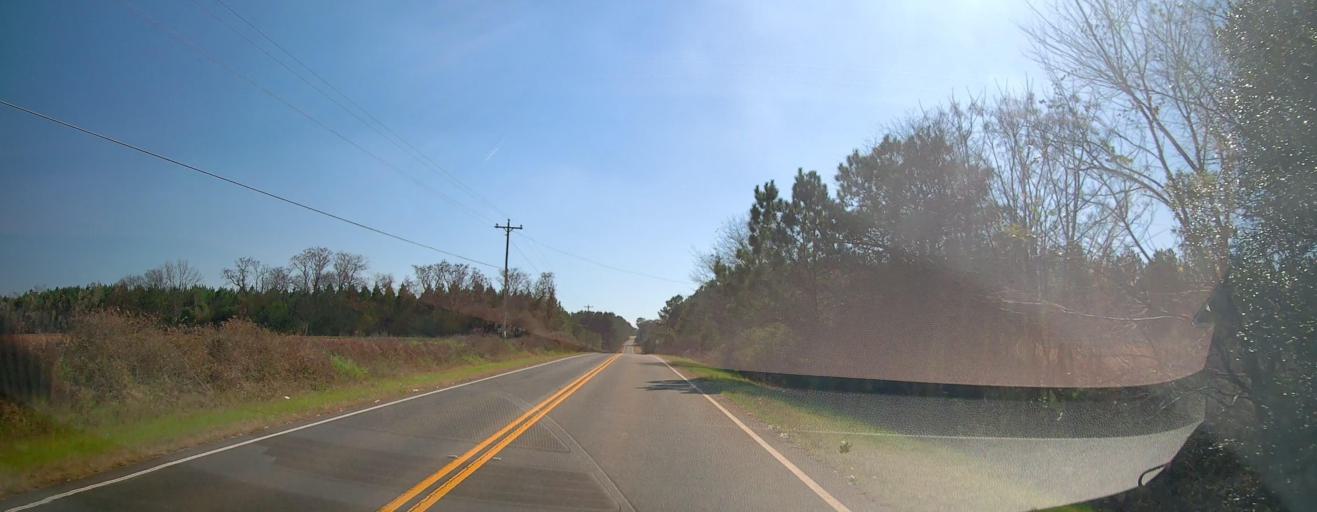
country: US
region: Georgia
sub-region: Macon County
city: Montezuma
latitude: 32.3269
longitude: -84.0222
